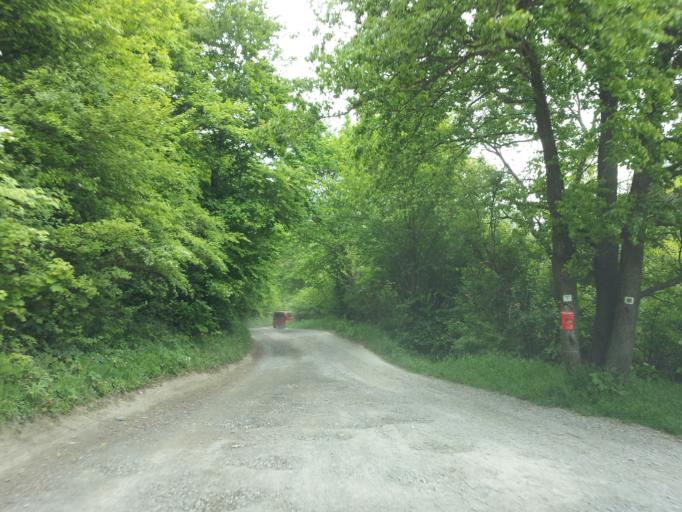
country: HU
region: Baranya
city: Hosszuheteny
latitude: 46.1752
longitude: 18.3482
